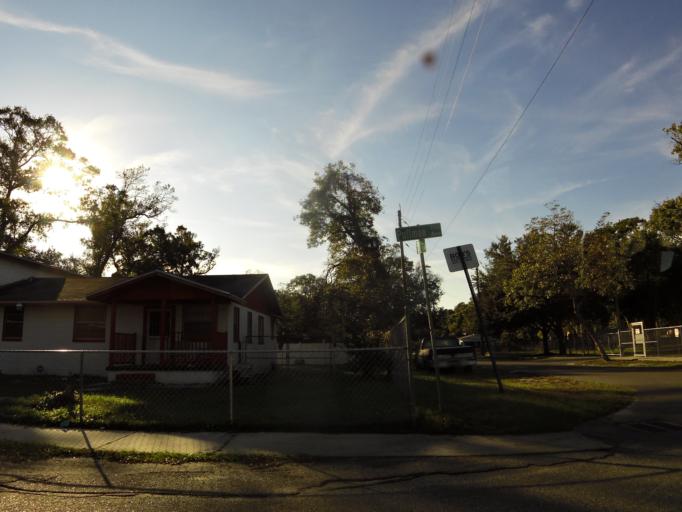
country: US
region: Florida
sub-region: Duval County
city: Jacksonville
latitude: 30.3526
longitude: -81.6899
